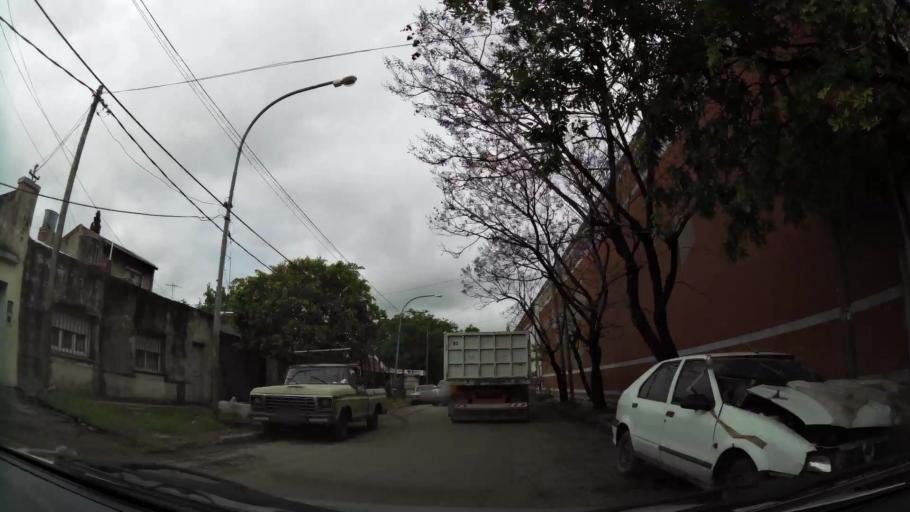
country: AR
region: Buenos Aires
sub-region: Partido de Lanus
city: Lanus
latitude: -34.7319
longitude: -58.3808
